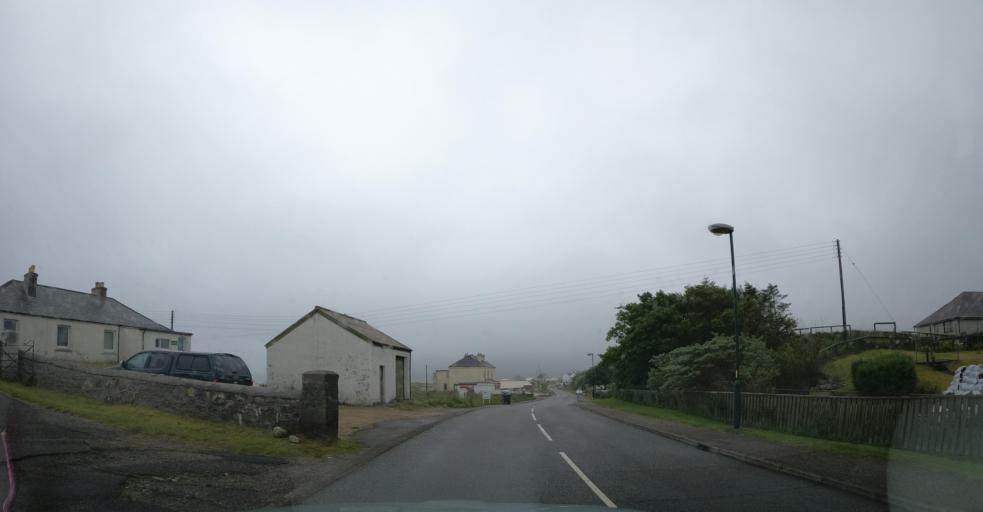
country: GB
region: Scotland
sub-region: Eilean Siar
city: Isle of North Uist
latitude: 57.6005
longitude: -7.1613
